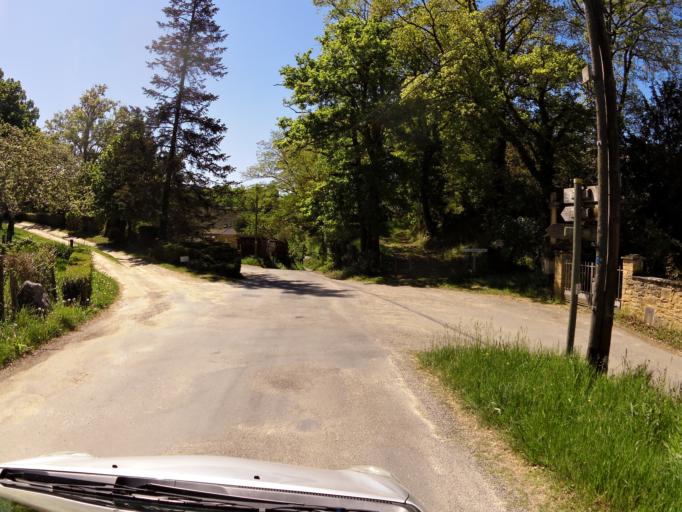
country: FR
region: Aquitaine
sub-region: Departement de la Dordogne
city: Domme
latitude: 44.7959
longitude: 1.2185
